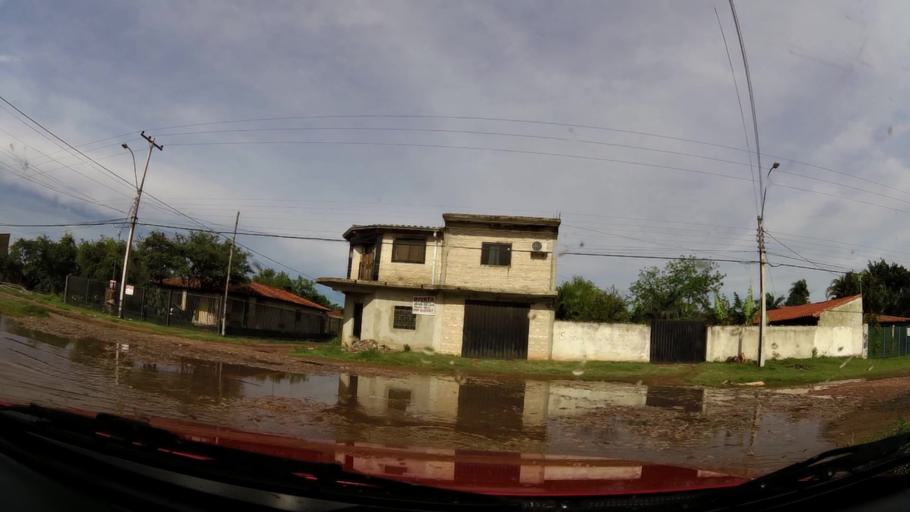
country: PY
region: Central
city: Limpio
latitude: -25.1677
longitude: -57.4896
